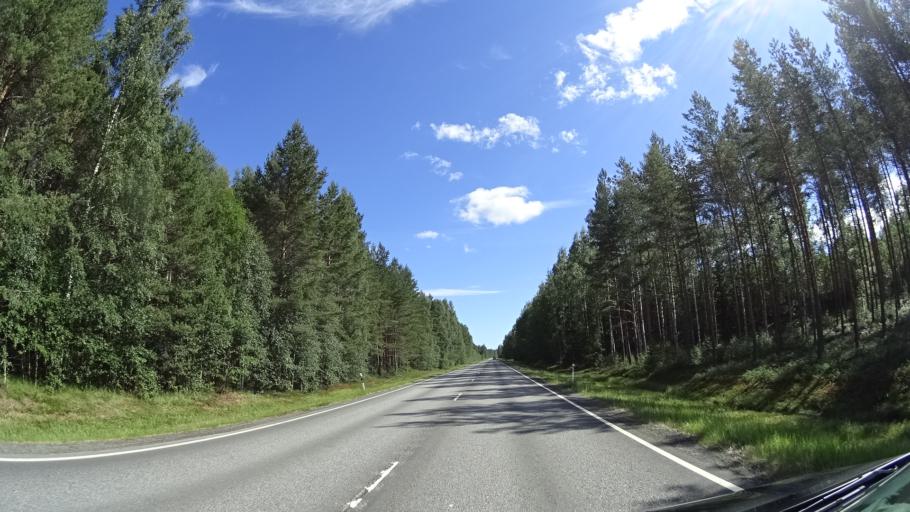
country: FI
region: Pirkanmaa
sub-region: Luoteis-Pirkanmaa
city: Kihnioe
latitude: 62.2114
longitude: 23.2452
